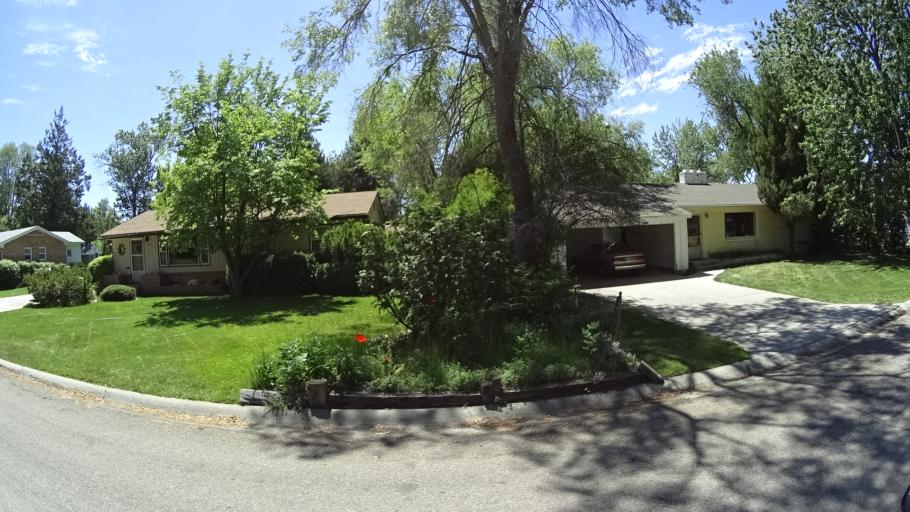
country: US
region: Idaho
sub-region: Ada County
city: Garden City
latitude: 43.5989
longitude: -116.2275
